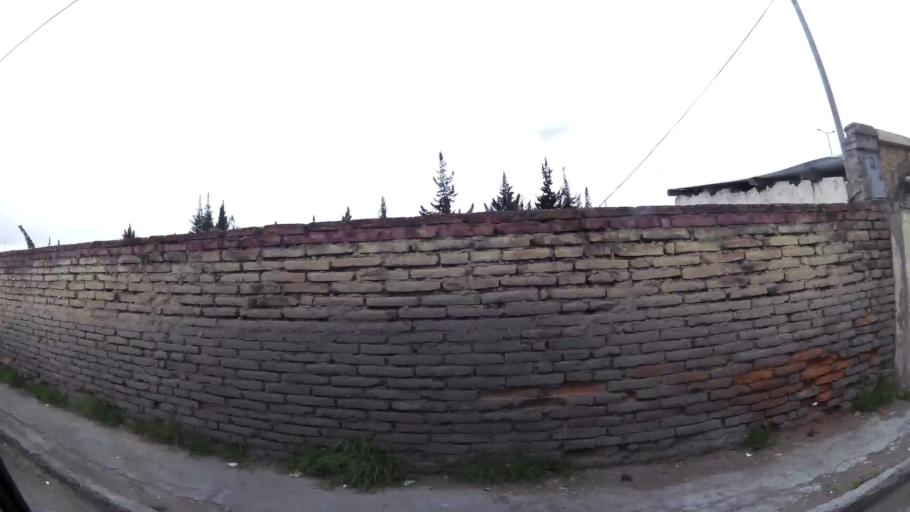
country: EC
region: Cotopaxi
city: Latacunga
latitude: -0.9329
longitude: -78.6199
